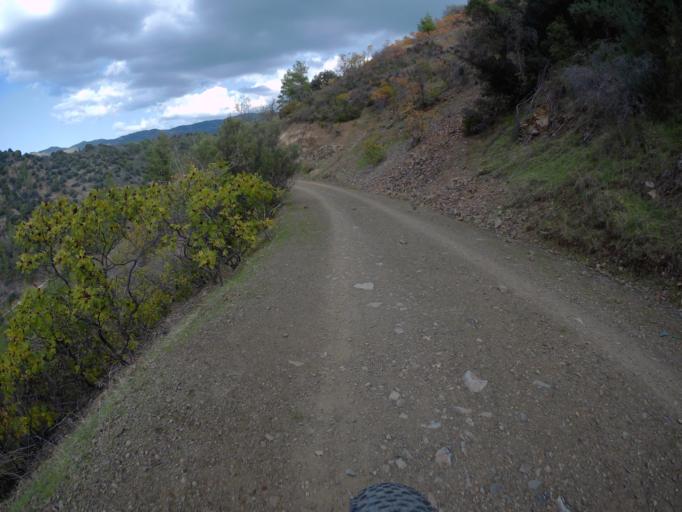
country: CY
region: Lefkosia
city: Kakopetria
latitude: 34.9172
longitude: 32.7887
